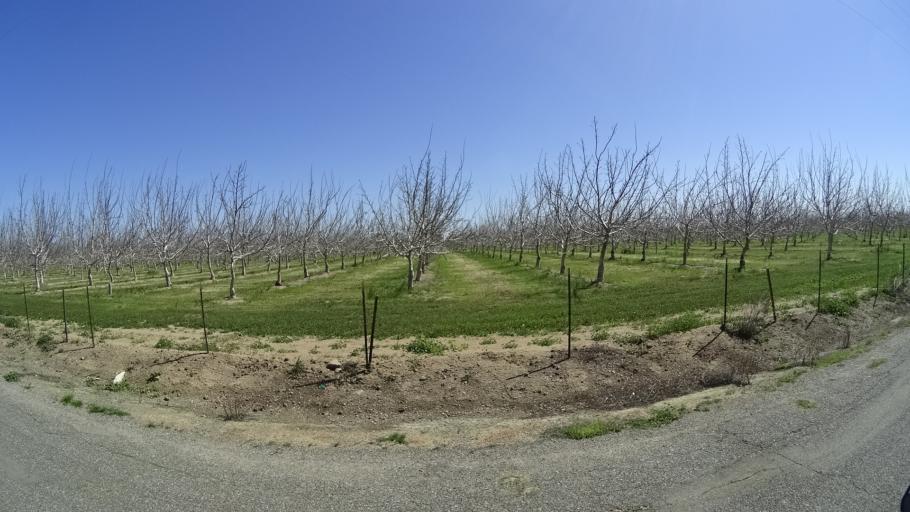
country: US
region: California
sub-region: Glenn County
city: Orland
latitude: 39.6848
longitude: -122.2342
